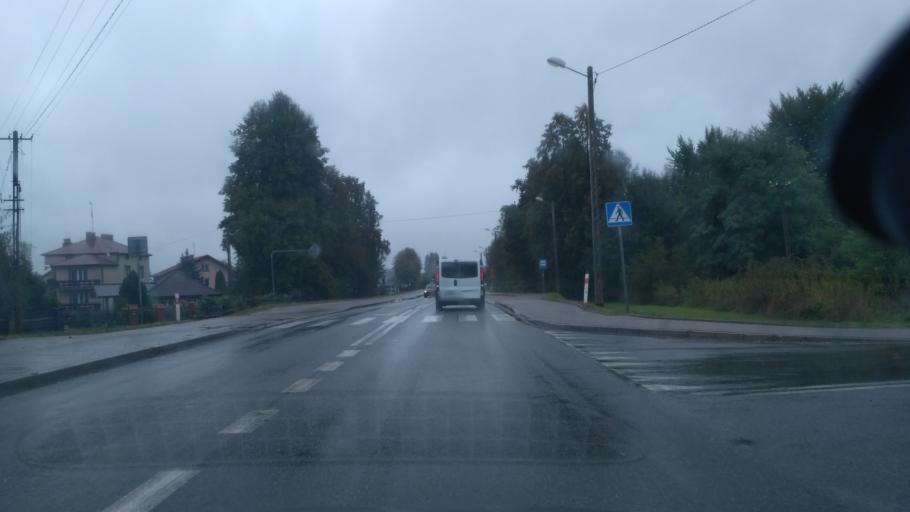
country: PL
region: Subcarpathian Voivodeship
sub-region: Powiat debicki
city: Debica
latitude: 50.0562
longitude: 21.4485
